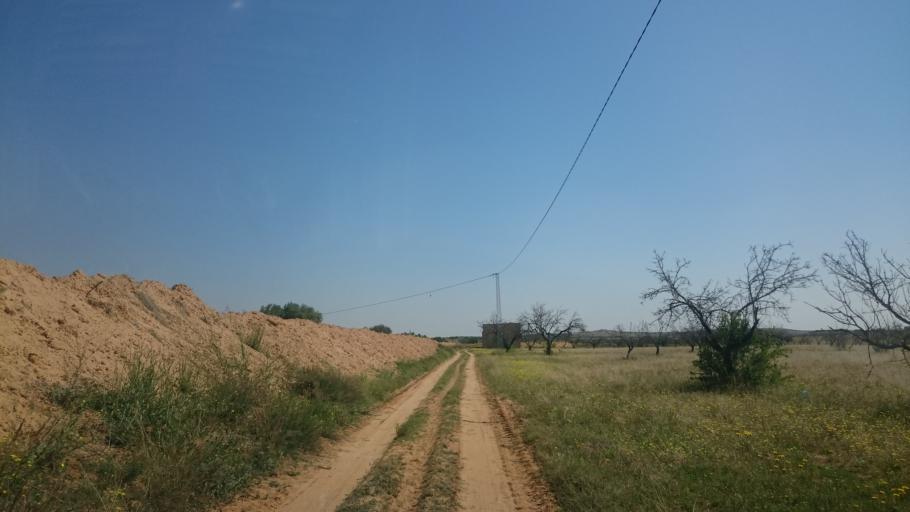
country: TN
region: Safaqis
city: Sfax
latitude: 34.7984
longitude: 10.5591
